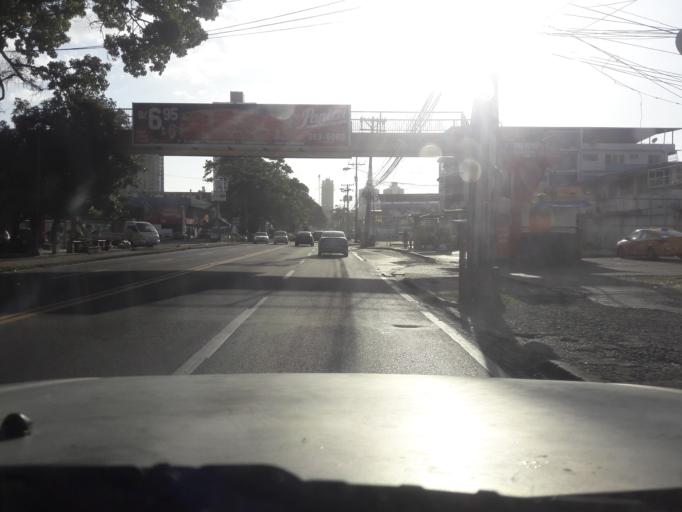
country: PA
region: Panama
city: Panama
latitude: 9.0135
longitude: -79.5007
